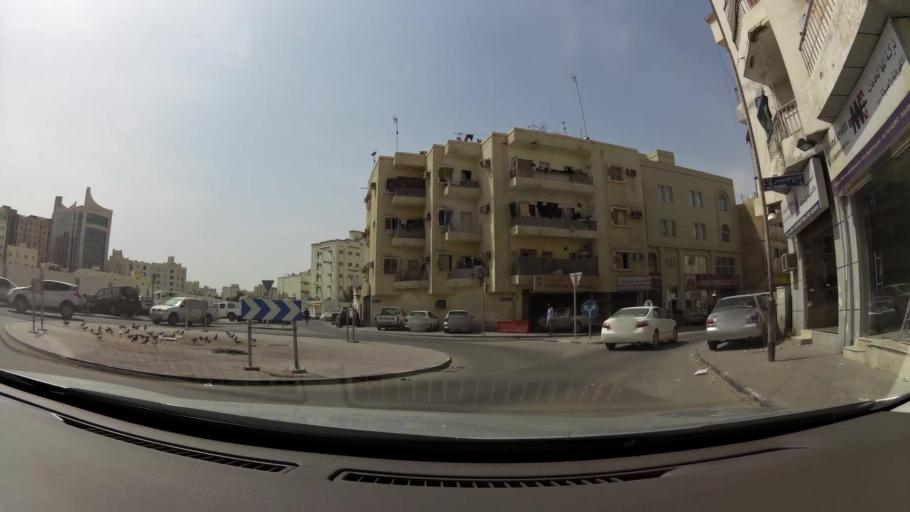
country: QA
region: Baladiyat ad Dawhah
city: Doha
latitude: 25.2794
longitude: 51.5402
